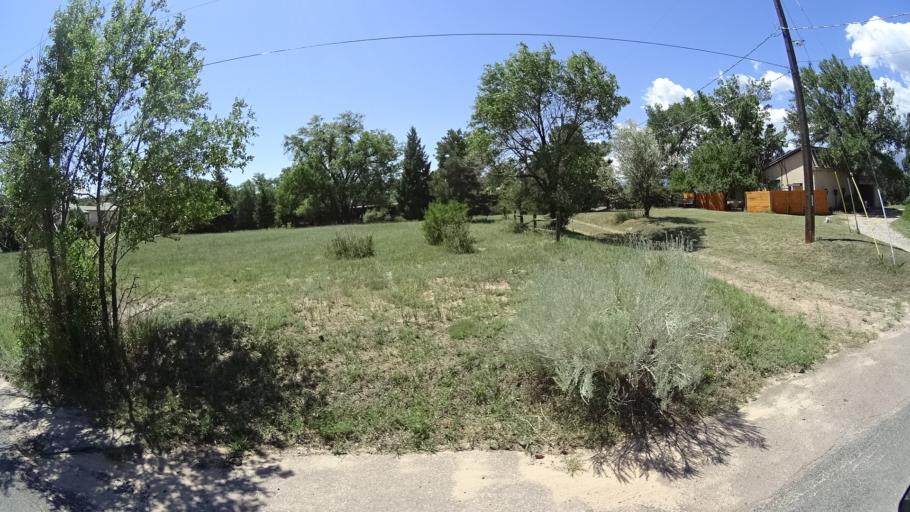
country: US
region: Colorado
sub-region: El Paso County
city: Colorado Springs
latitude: 38.9028
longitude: -104.8078
